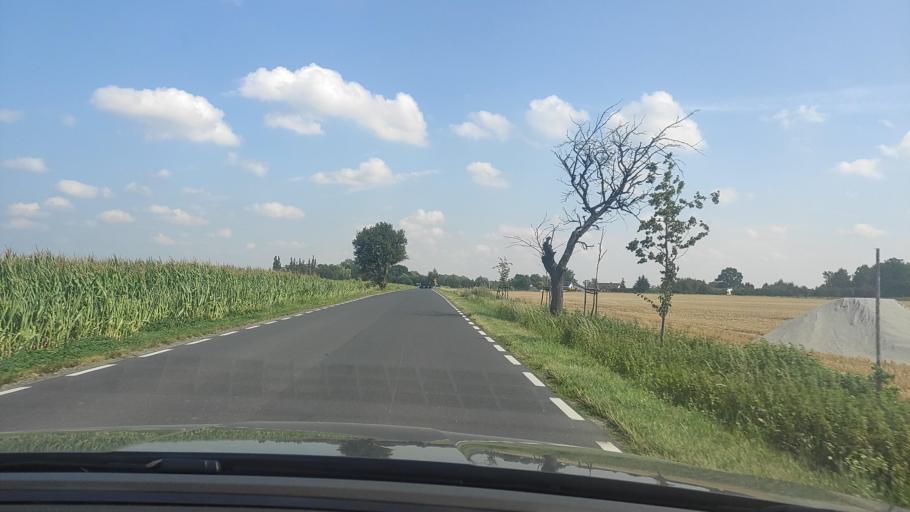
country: PL
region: Greater Poland Voivodeship
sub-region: Powiat poznanski
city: Kostrzyn
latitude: 52.4398
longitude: 17.1672
